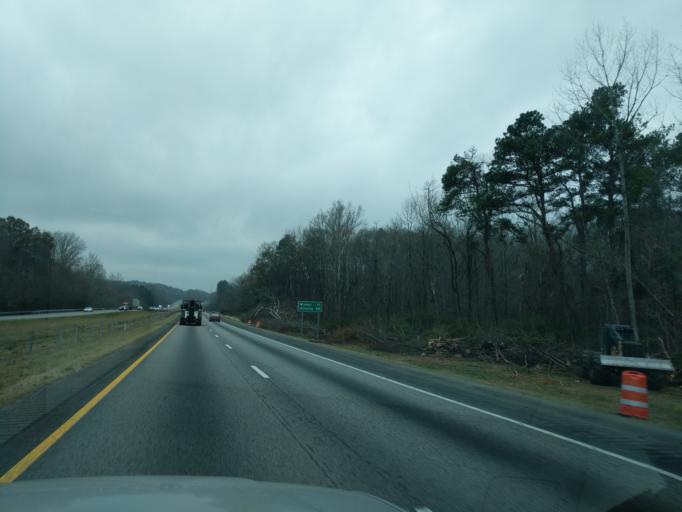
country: US
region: Georgia
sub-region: Jackson County
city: Jefferson
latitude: 34.1452
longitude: -83.6570
